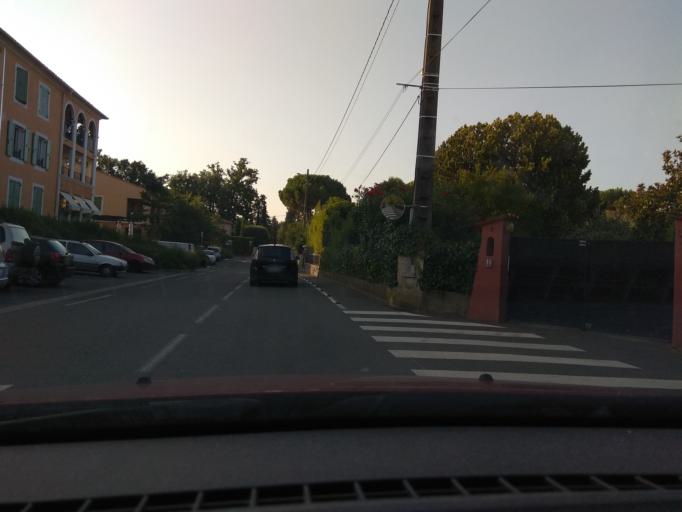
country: FR
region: Provence-Alpes-Cote d'Azur
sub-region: Departement des Alpes-Maritimes
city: Le Rouret
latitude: 43.6662
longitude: 7.0476
